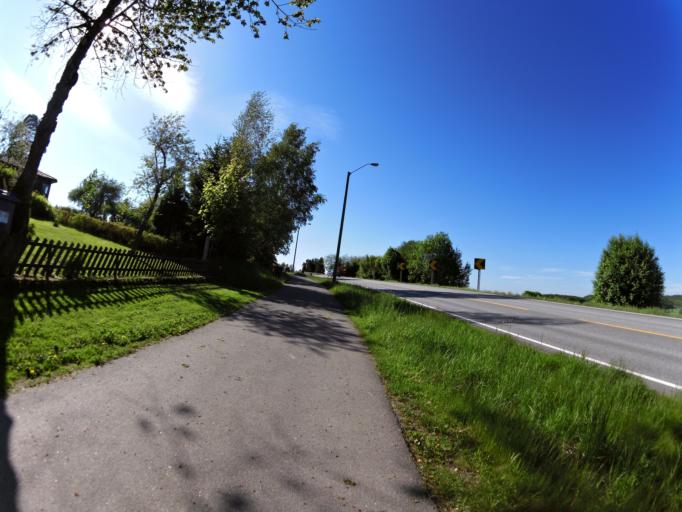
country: NO
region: Ostfold
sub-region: Sarpsborg
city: Sarpsborg
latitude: 59.2251
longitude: 11.0530
